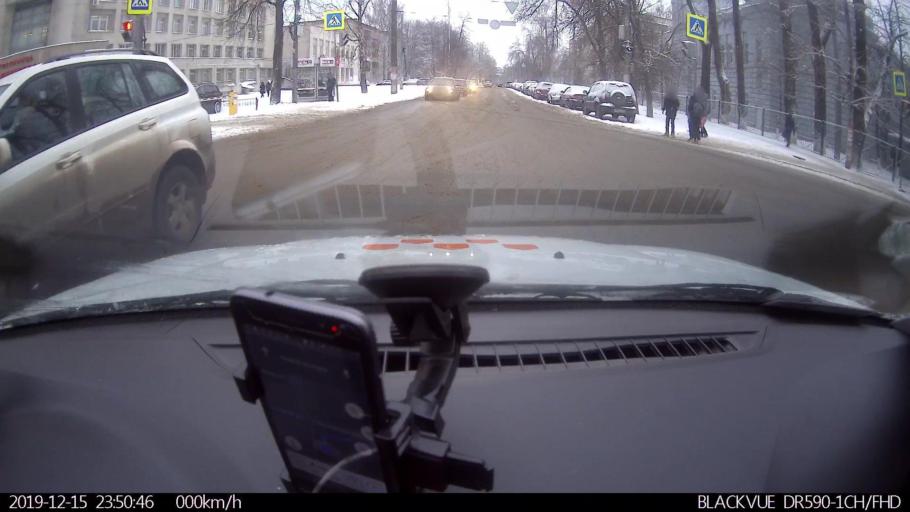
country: RU
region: Nizjnij Novgorod
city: Nizhniy Novgorod
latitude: 56.3062
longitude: 43.9897
